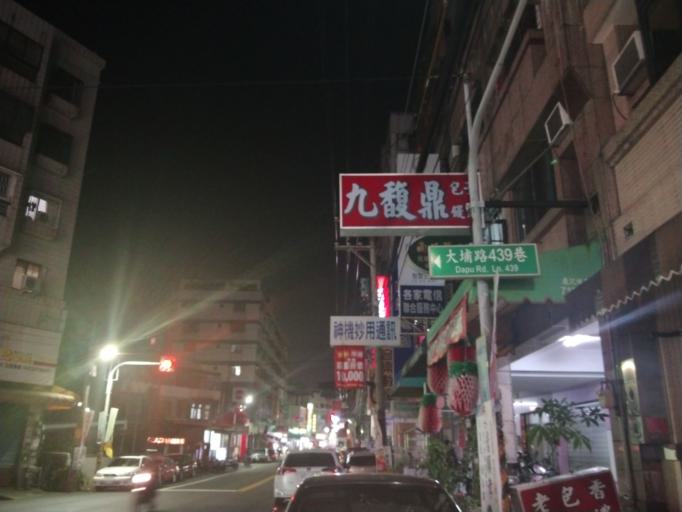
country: TW
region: Taiwan
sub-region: Changhua
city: Chang-hua
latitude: 24.0632
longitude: 120.5435
